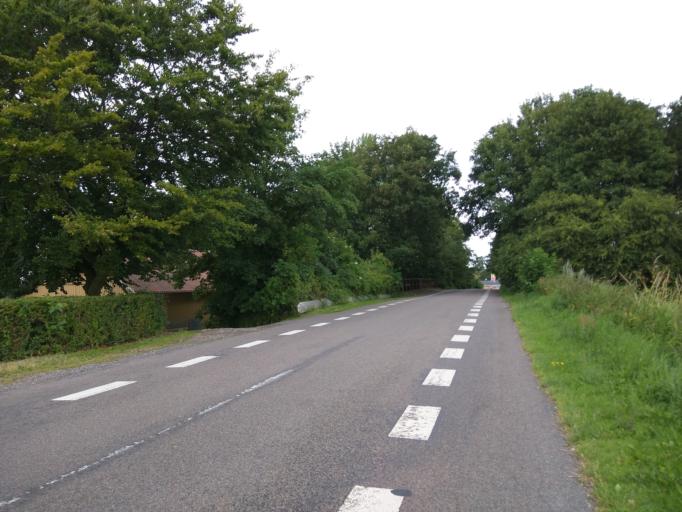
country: DK
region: Zealand
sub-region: Kalundborg Kommune
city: Svebolle
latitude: 55.7109
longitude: 11.3027
